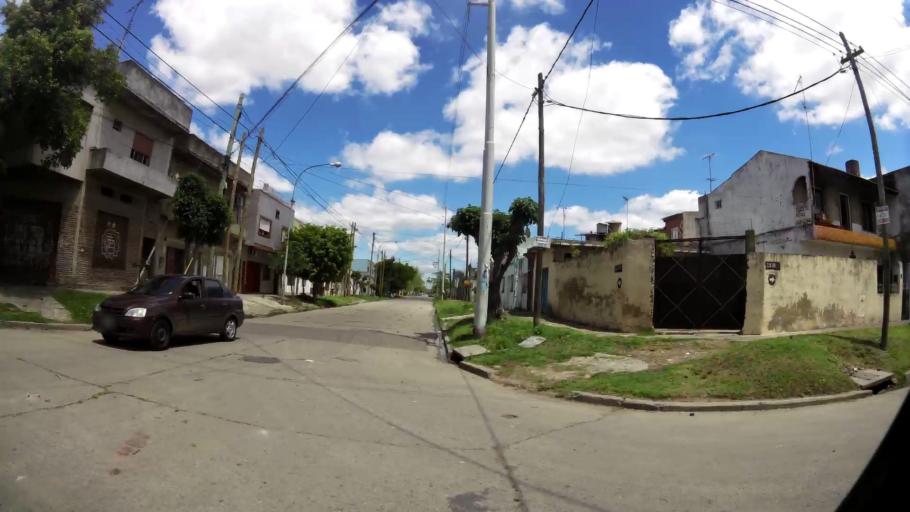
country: AR
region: Buenos Aires
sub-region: Partido de Lanus
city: Lanus
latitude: -34.7135
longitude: -58.4230
